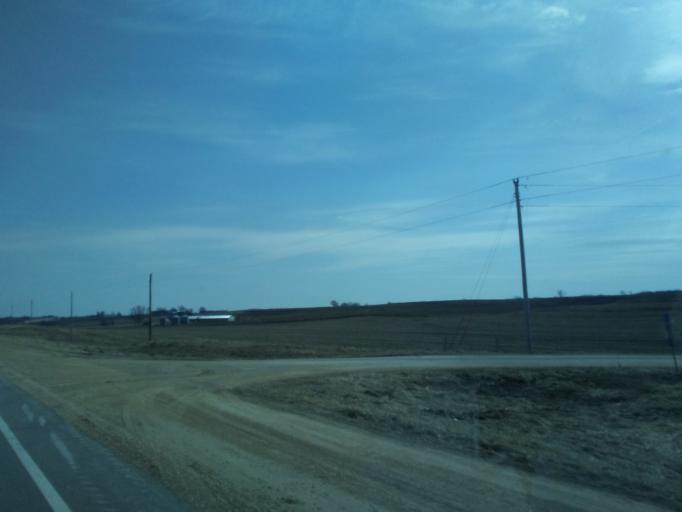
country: US
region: Iowa
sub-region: Winneshiek County
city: Decorah
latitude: 43.4001
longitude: -91.8441
